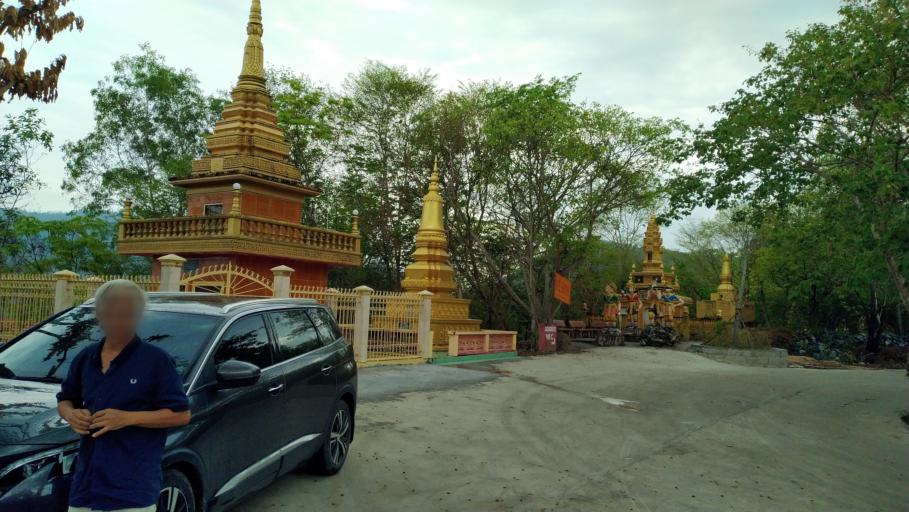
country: VN
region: An Giang
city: Tri Ton
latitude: 10.4147
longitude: 104.9925
